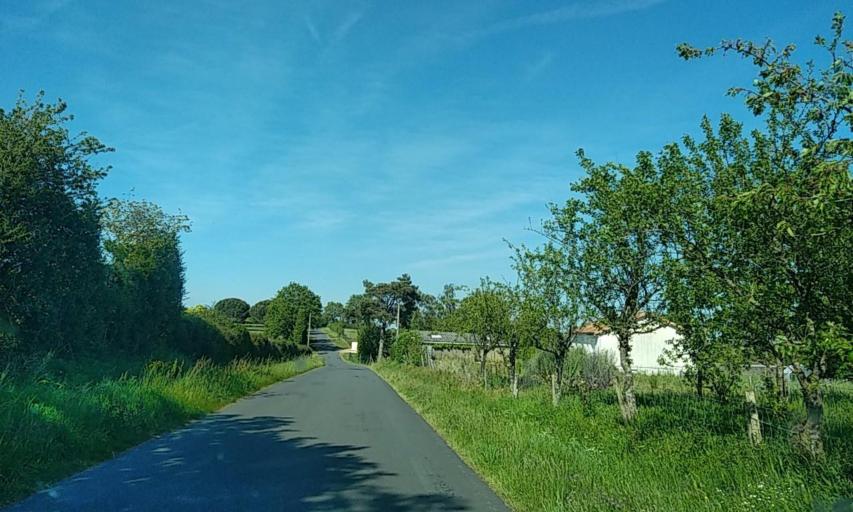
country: FR
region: Poitou-Charentes
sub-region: Departement des Deux-Sevres
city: Boisme
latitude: 46.7856
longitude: -0.3980
